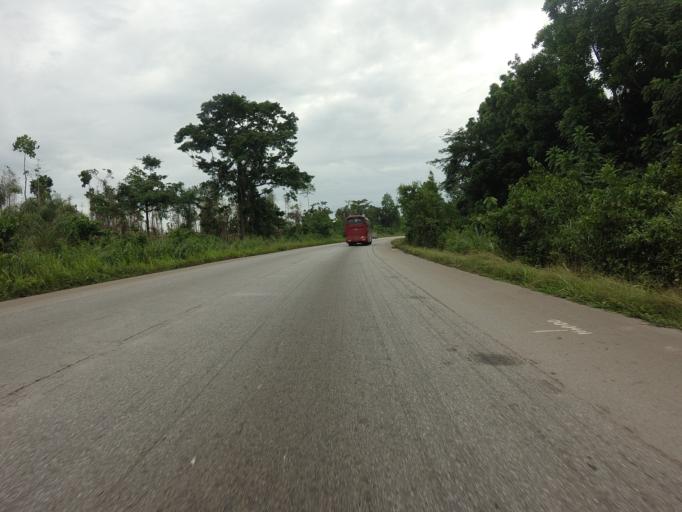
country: GH
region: Eastern
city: Nkawkaw
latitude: 6.6000
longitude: -0.9762
